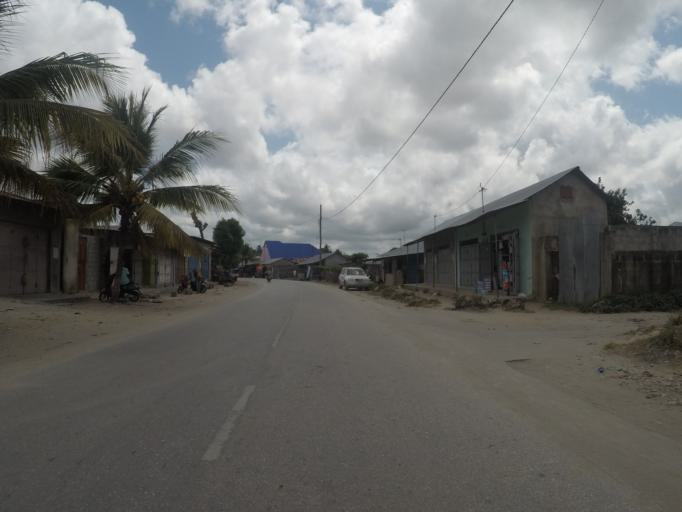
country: TZ
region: Zanzibar Urban/West
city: Zanzibar
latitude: -6.1934
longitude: 39.2445
